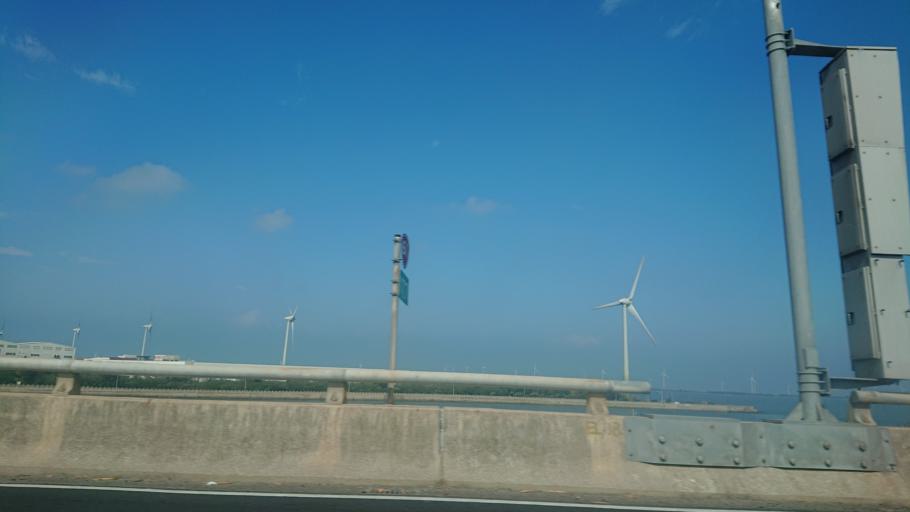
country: TW
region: Taiwan
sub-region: Changhua
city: Chang-hua
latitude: 24.0822
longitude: 120.4206
